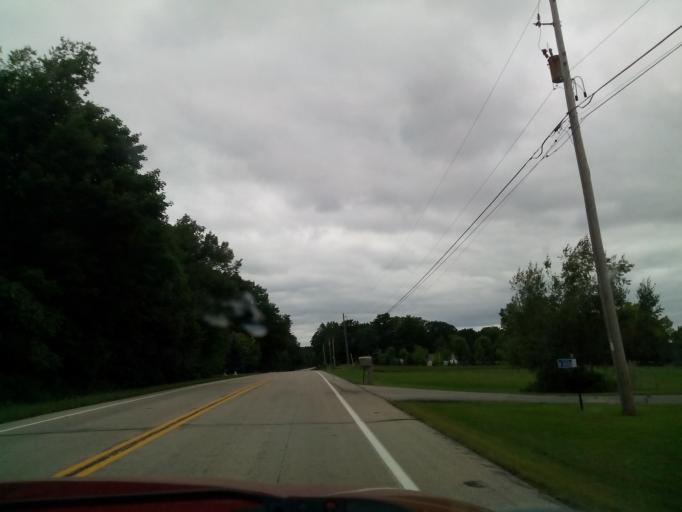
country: US
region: Wisconsin
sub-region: Outagamie County
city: Hortonville
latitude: 44.3588
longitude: -88.5924
